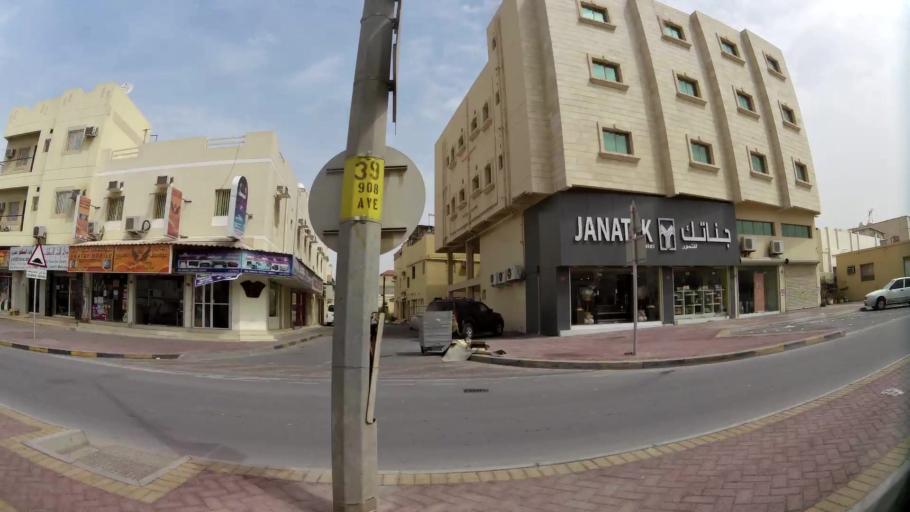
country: BH
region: Northern
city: Ar Rifa'
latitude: 26.1215
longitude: 50.5413
